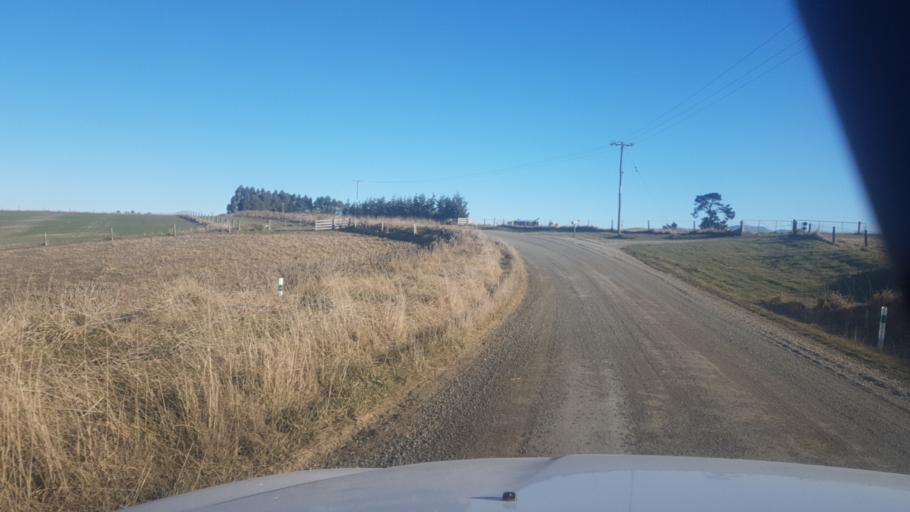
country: NZ
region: Canterbury
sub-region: Timaru District
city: Pleasant Point
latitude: -44.3470
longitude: 171.0748
